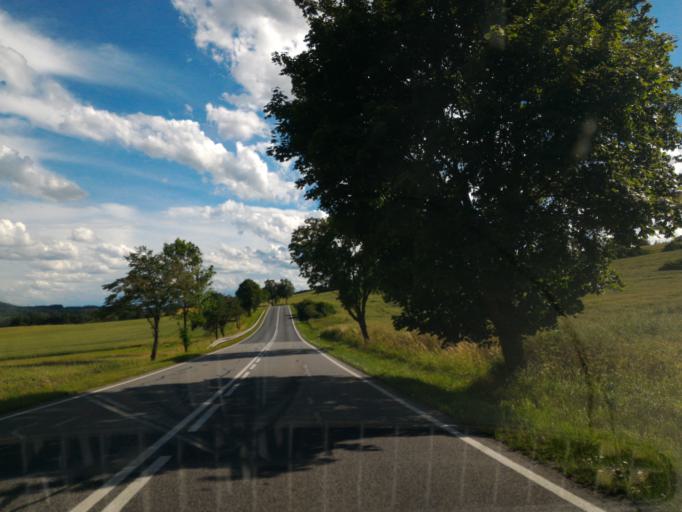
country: CZ
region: Vysocina
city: Dolni Cerekev
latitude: 49.3472
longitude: 15.4847
